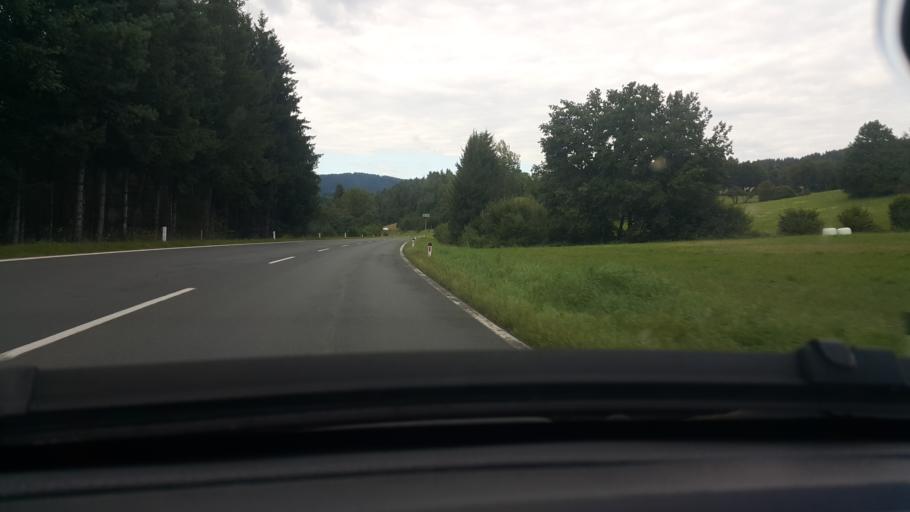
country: AT
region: Carinthia
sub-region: Politischer Bezirk Feldkirchen
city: Feldkirchen in Karnten
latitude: 46.7026
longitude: 14.1190
